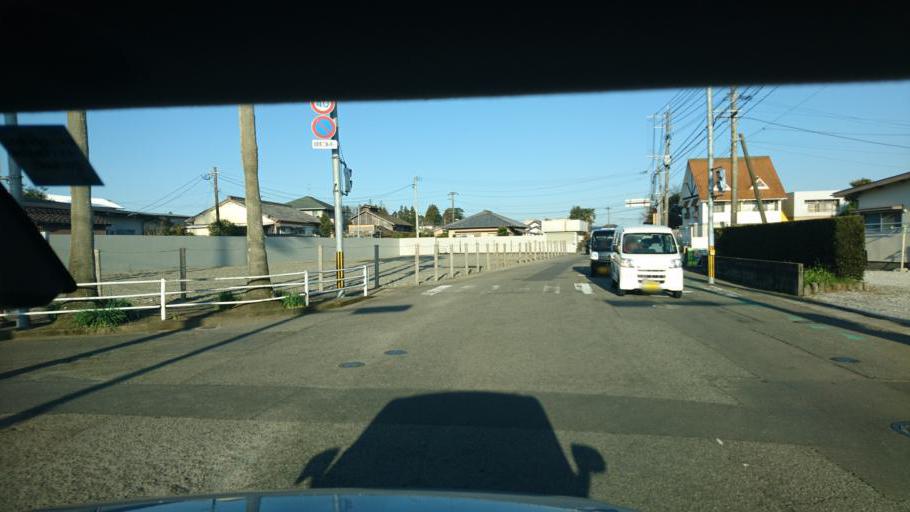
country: JP
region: Miyazaki
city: Miyazaki-shi
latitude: 31.8438
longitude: 131.3997
